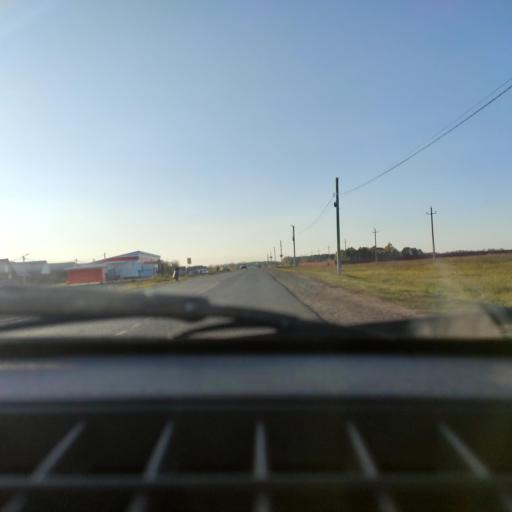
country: RU
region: Bashkortostan
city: Avdon
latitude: 54.6588
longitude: 55.7436
